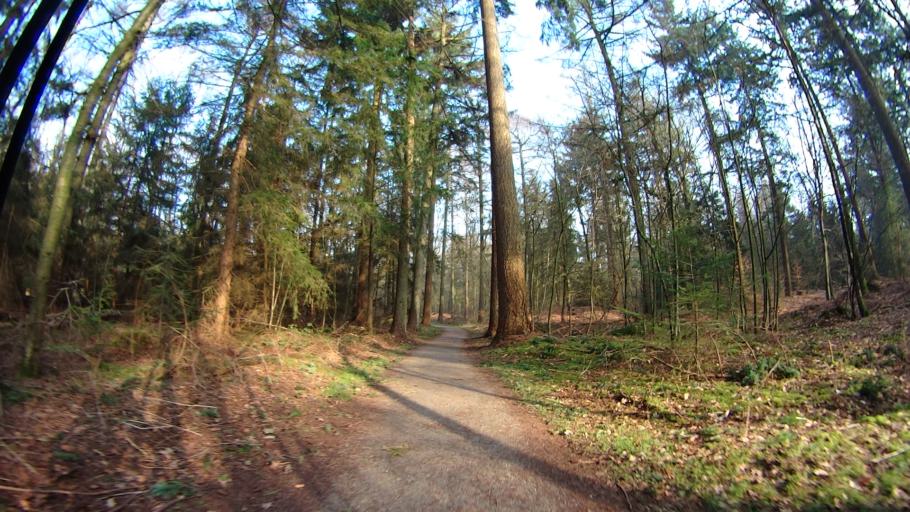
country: NL
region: Drenthe
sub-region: Gemeente Emmen
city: Emmen
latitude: 52.7922
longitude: 6.9116
